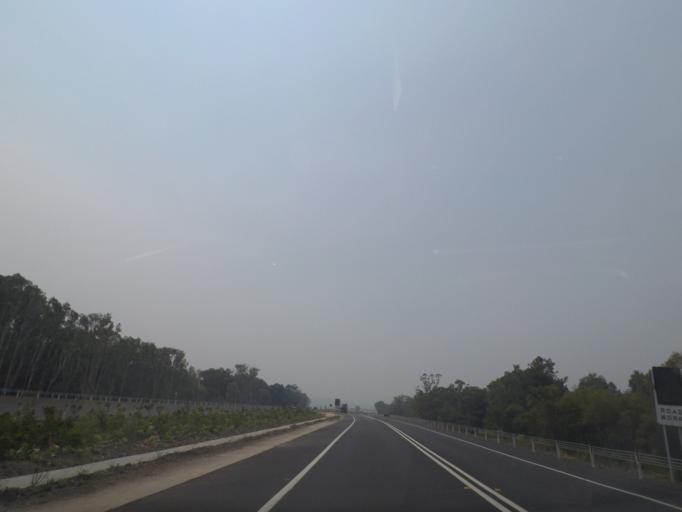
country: AU
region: New South Wales
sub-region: Ballina
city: Ballina
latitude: -28.9110
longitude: 153.4788
